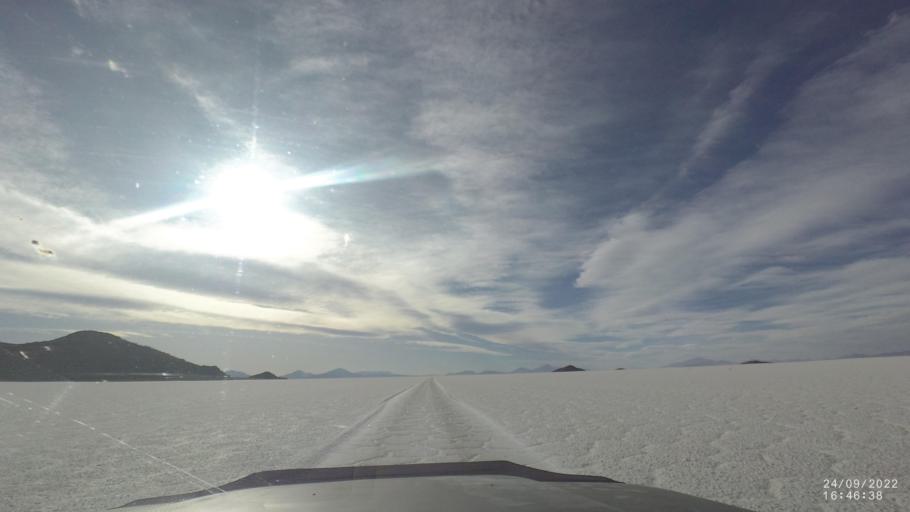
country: BO
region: Potosi
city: Colchani
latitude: -20.1361
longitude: -67.7930
